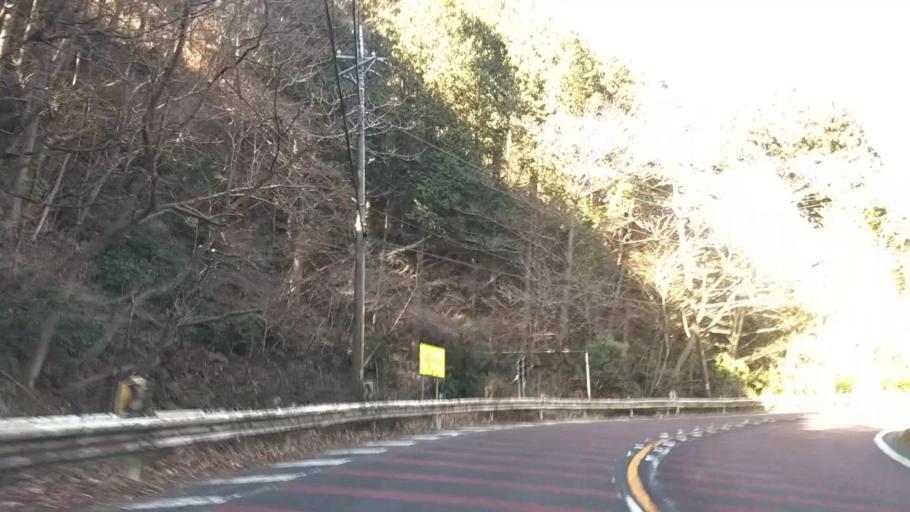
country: JP
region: Tokyo
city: Hachioji
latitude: 35.6193
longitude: 139.2372
